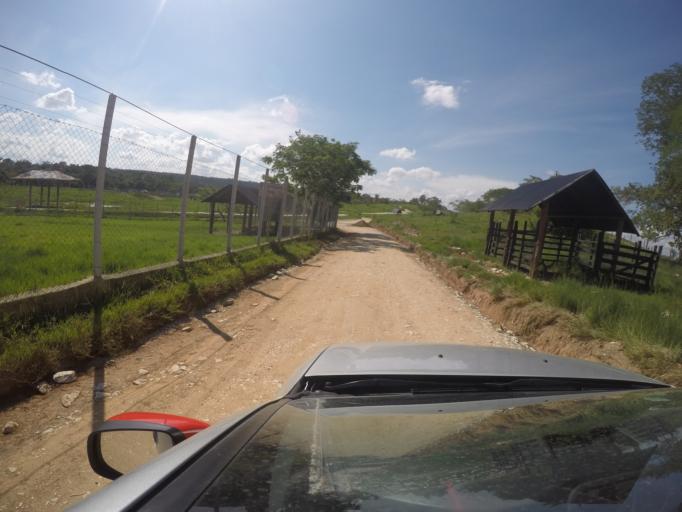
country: CO
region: Antioquia
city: Puerto Triunfo
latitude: 5.9309
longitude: -74.7231
